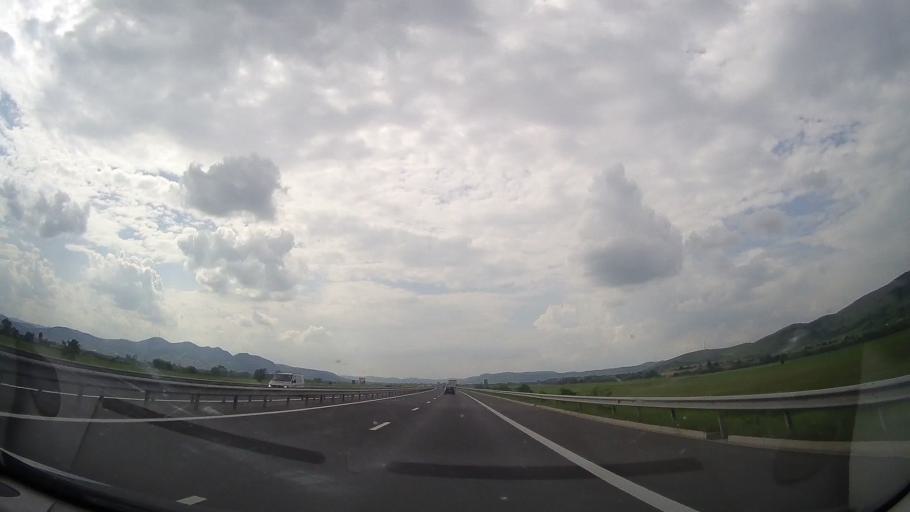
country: RO
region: Hunedoara
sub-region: Comuna Harau
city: Harau
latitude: 45.8851
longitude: 22.9837
